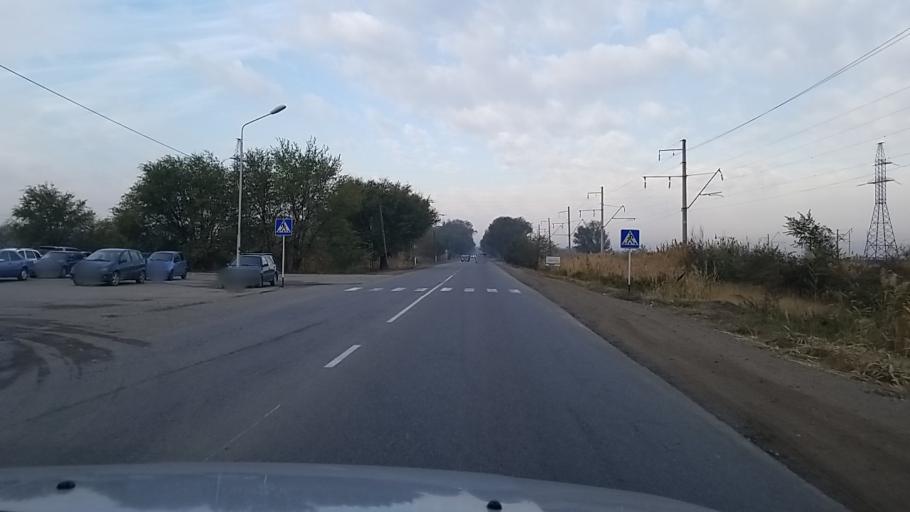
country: KZ
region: Almaty Oblysy
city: Burunday
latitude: 43.3578
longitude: 76.7818
